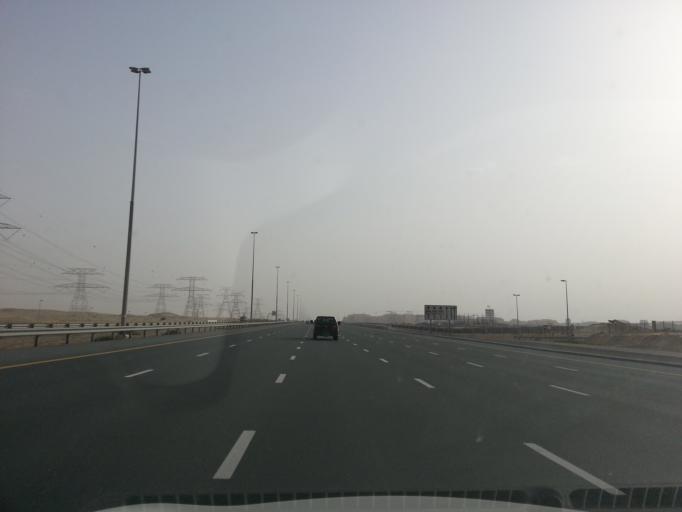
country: AE
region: Dubai
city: Dubai
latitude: 25.0118
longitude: 55.2699
